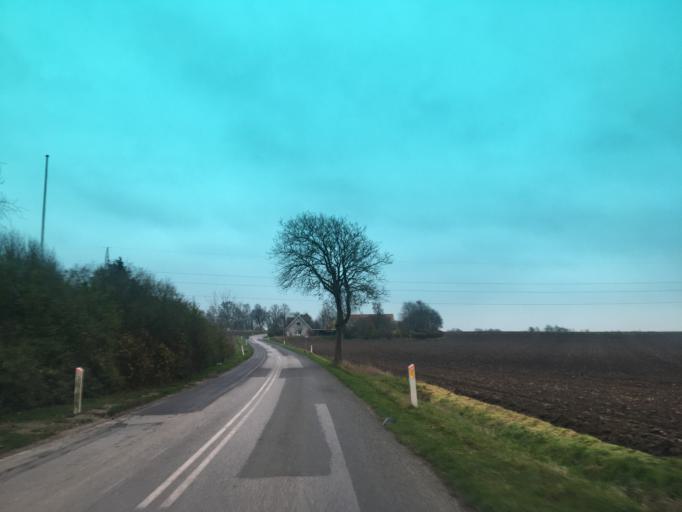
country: DK
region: Zealand
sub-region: Slagelse Kommune
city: Skaelskor
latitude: 55.2493
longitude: 11.4213
